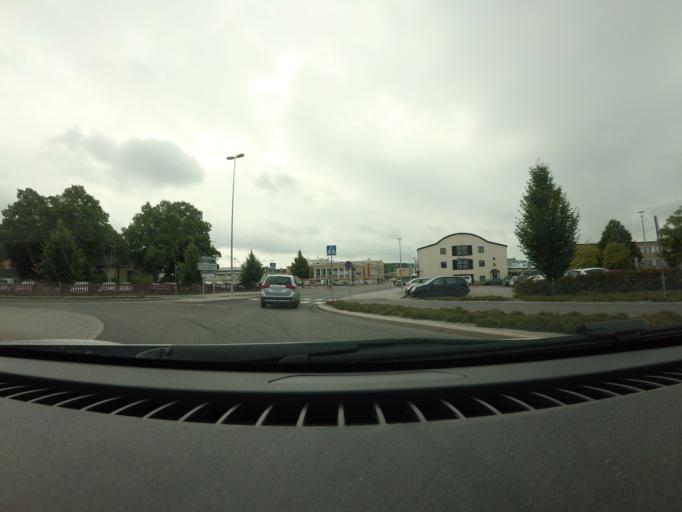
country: FI
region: Varsinais-Suomi
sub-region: Turku
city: Turku
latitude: 60.4357
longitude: 22.2234
